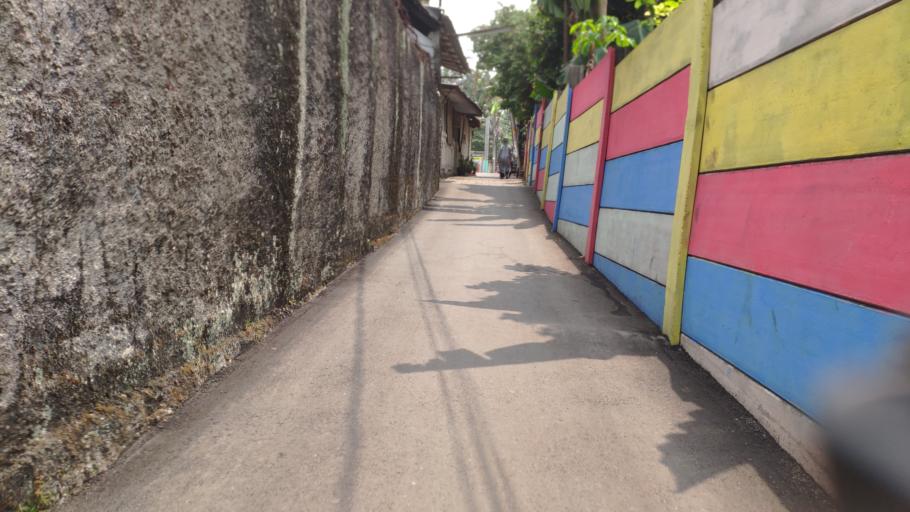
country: ID
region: Jakarta Raya
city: Jakarta
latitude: -6.3057
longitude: 106.8345
